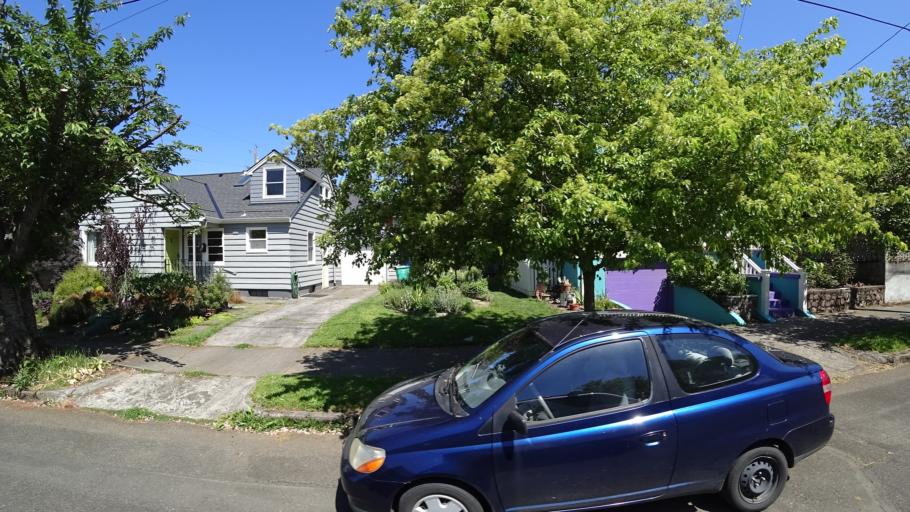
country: US
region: Oregon
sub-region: Multnomah County
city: Portland
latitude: 45.5073
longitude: -122.6333
